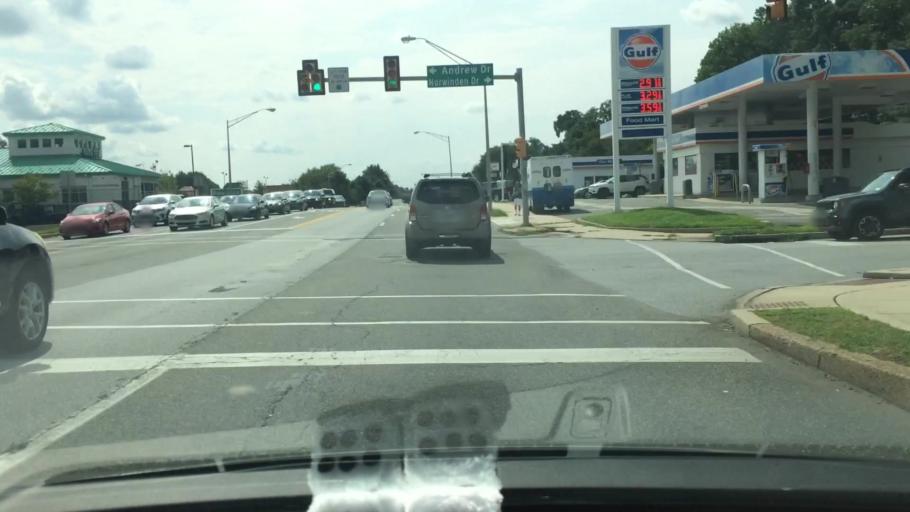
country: US
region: Pennsylvania
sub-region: Delaware County
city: Springfield
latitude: 39.9216
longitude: -75.3209
